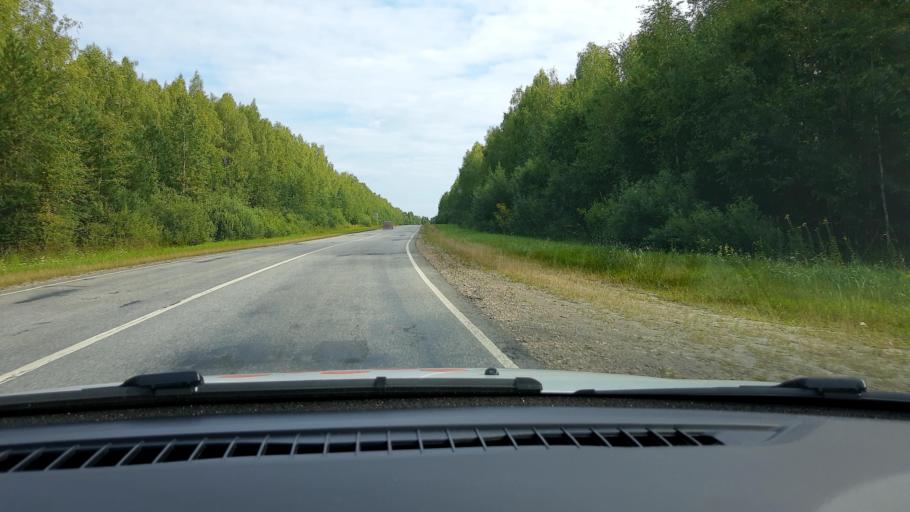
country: RU
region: Nizjnij Novgorod
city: Krasnyye Baki
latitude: 57.0053
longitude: 45.1117
